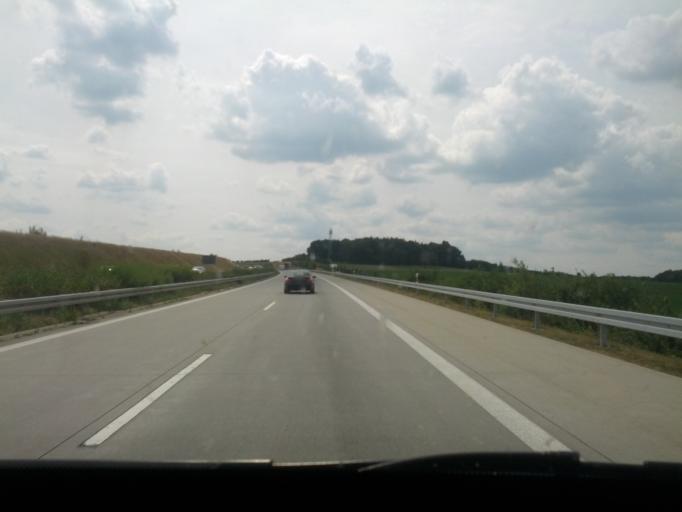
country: DE
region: Saxony
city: Liebstadt
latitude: 50.8867
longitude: 13.8791
